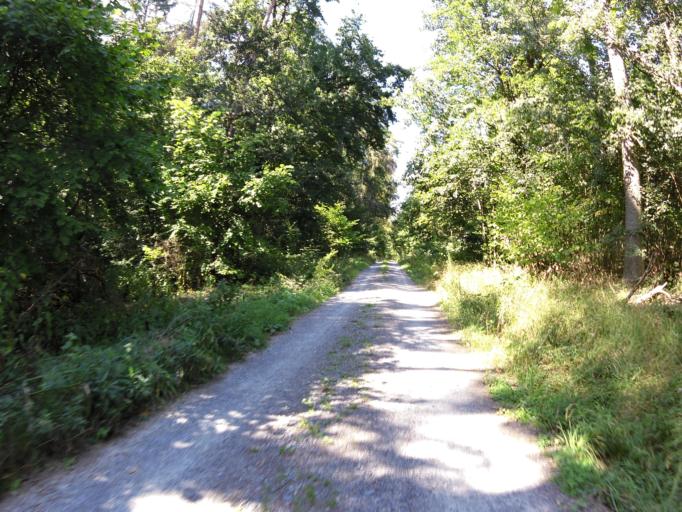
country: DE
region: Bavaria
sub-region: Regierungsbezirk Unterfranken
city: Guntersleben
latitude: 49.8573
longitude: 9.8865
